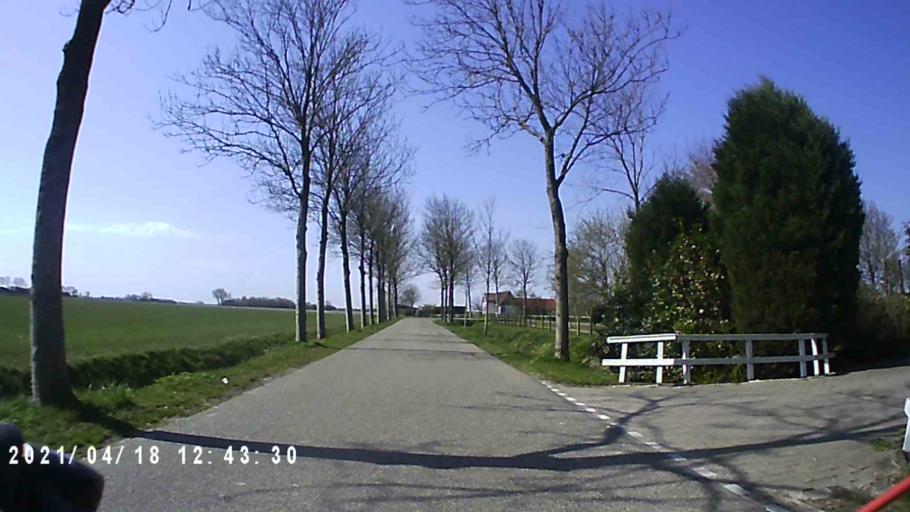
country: NL
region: Friesland
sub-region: Gemeente Dongeradeel
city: Anjum
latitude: 53.3626
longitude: 6.0609
